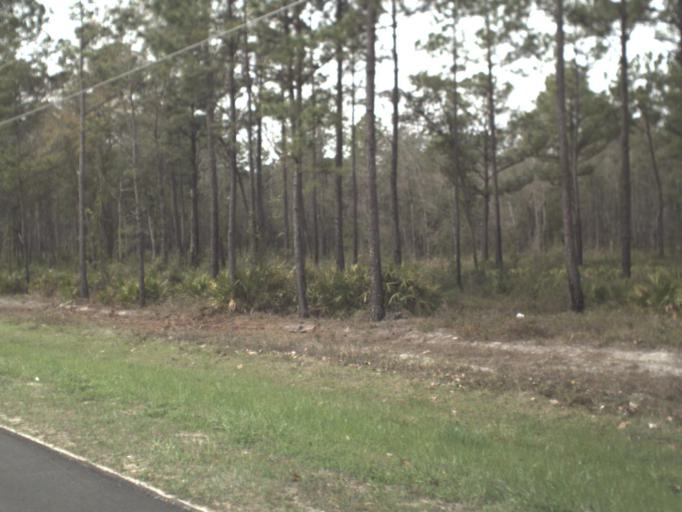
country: US
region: Florida
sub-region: Gadsden County
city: Midway
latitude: 30.4435
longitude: -84.4055
